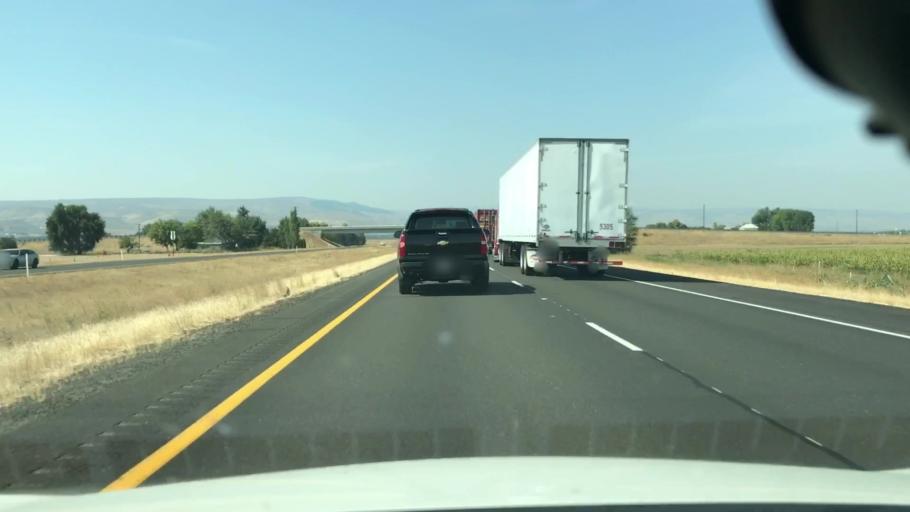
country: US
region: Washington
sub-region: Kittitas County
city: Ellensburg
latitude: 46.9694
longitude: -120.4935
